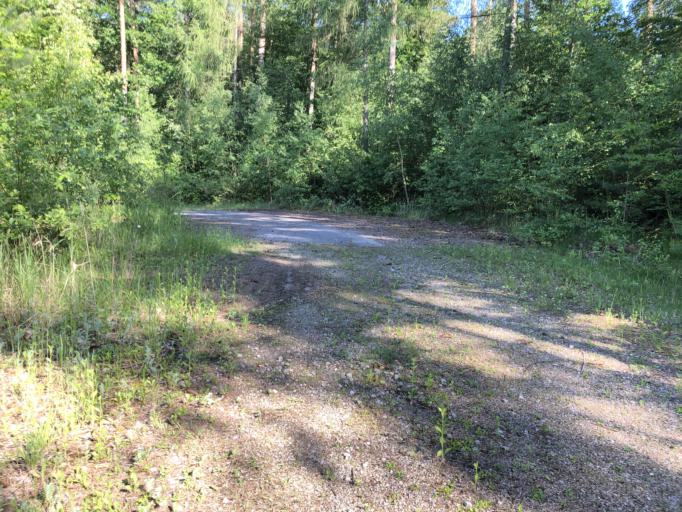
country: DE
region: Bavaria
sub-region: Upper Franconia
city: Memmelsdorf
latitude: 49.9151
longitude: 10.9600
